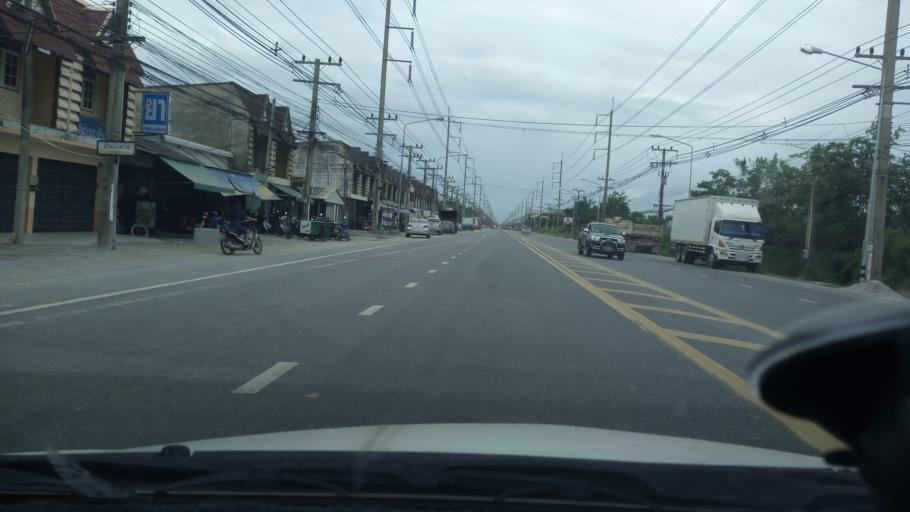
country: TH
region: Chon Buri
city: Phanat Nikhom
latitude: 13.4661
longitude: 101.1719
